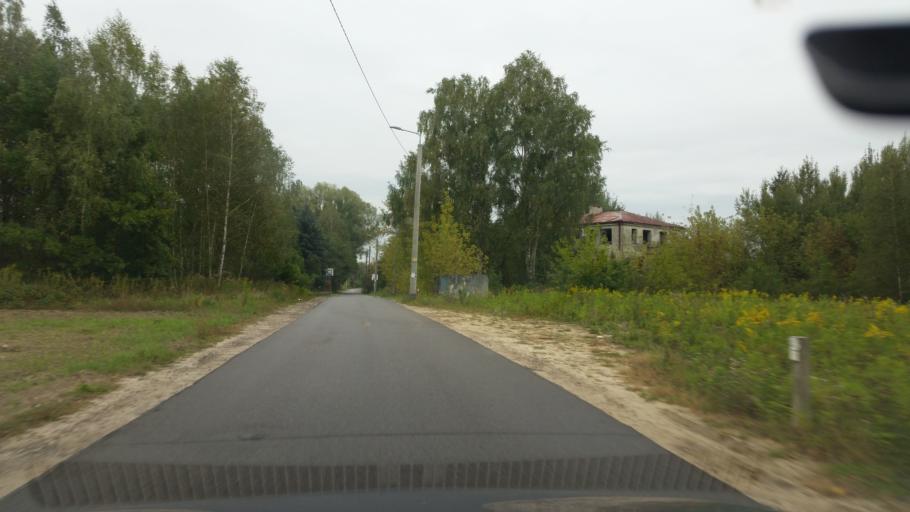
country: PL
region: Masovian Voivodeship
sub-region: Powiat piaseczynski
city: Konstancin-Jeziorna
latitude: 52.0875
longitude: 21.0831
